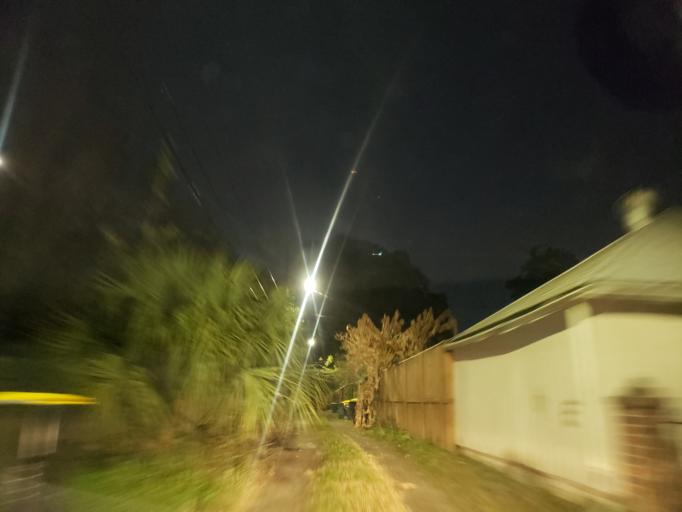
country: US
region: Georgia
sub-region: Chatham County
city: Savannah
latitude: 32.0438
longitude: -81.0951
